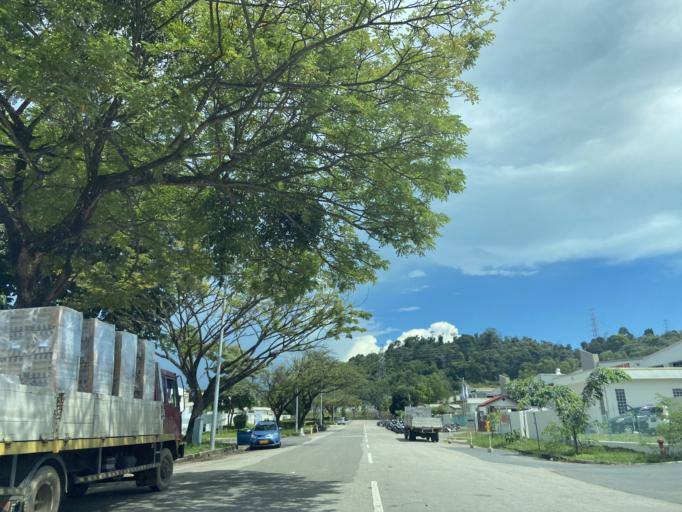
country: SG
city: Singapore
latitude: 1.0542
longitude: 104.0391
